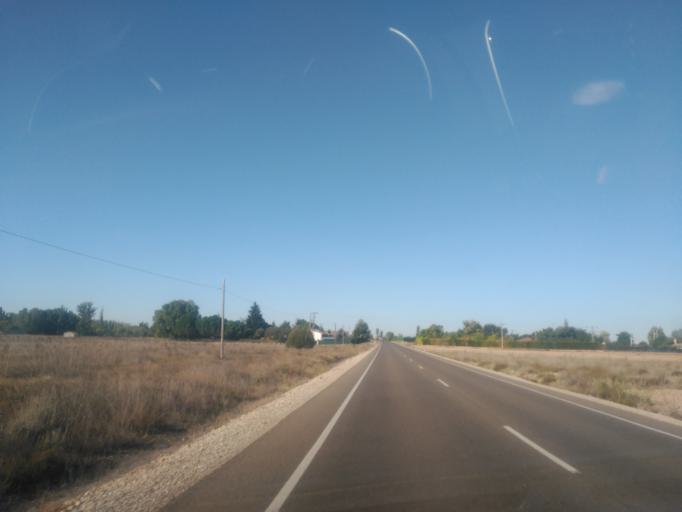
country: ES
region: Castille and Leon
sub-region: Provincia de Burgos
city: Fresnillo de las Duenas
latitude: 41.6862
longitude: -3.6214
